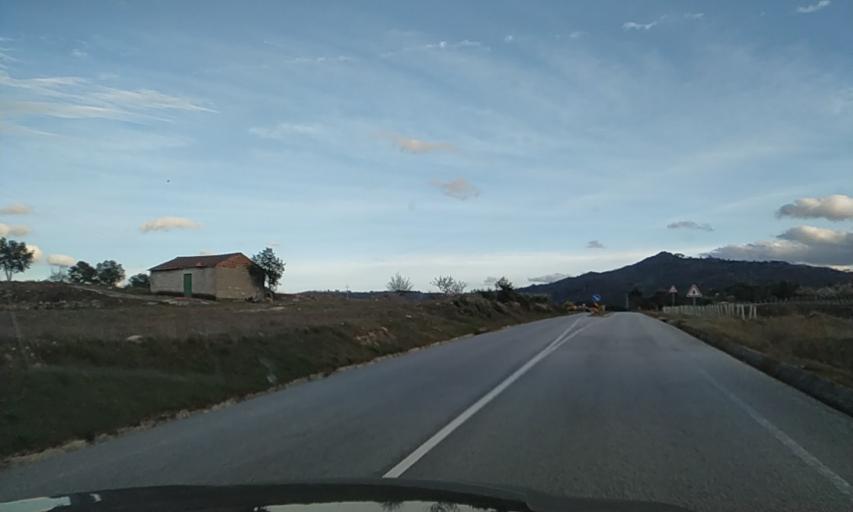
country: PT
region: Braganca
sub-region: Carrazeda de Ansiaes
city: Carrazeda de Anciaes
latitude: 41.2781
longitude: -7.3307
